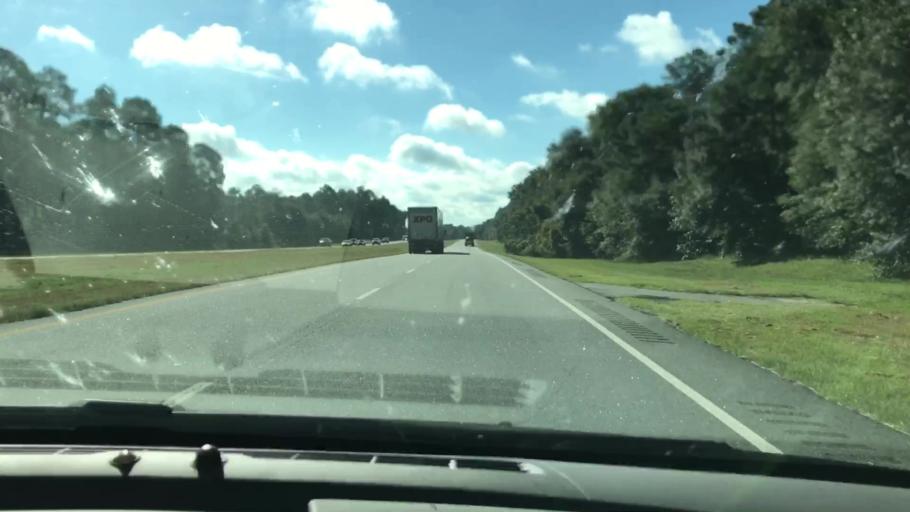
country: US
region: Georgia
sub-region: Dougherty County
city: Putney
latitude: 31.5621
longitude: -84.0125
